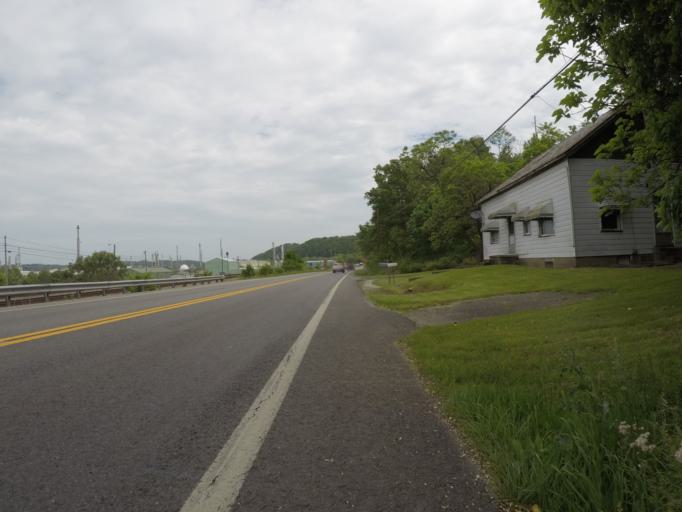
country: US
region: West Virginia
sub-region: Wayne County
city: Kenova
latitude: 38.3689
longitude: -82.5920
